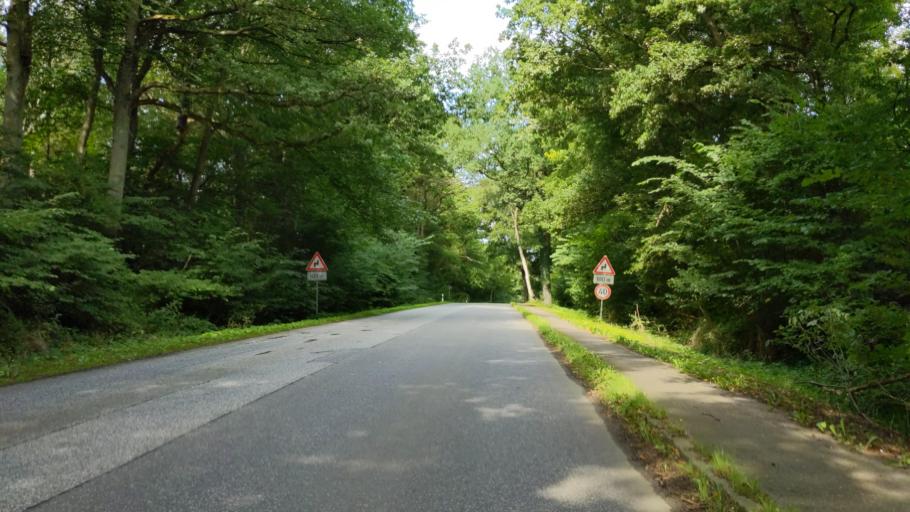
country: DE
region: Schleswig-Holstein
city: Susel
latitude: 54.0874
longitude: 10.6886
